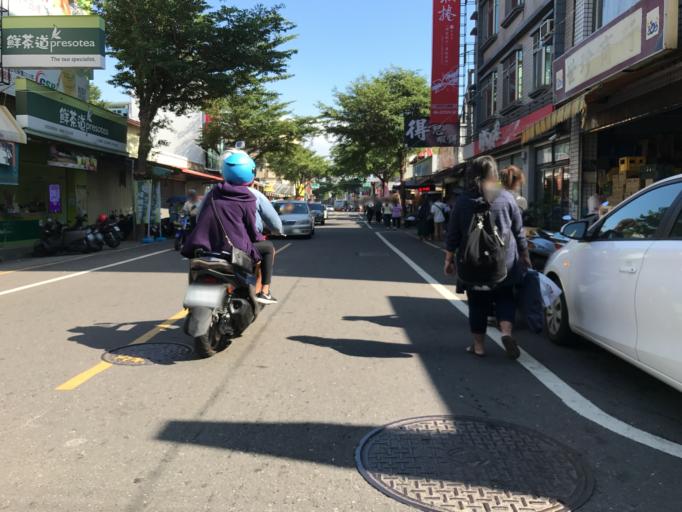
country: TW
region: Taiwan
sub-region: Tainan
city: Tainan
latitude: 23.0000
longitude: 120.1630
